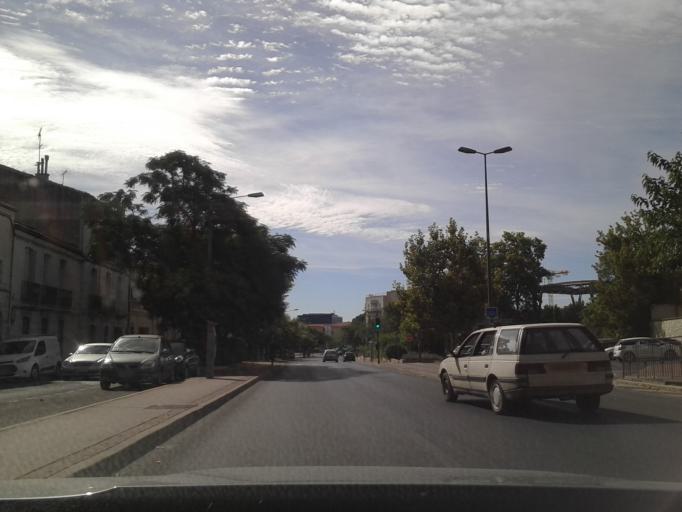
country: FR
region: Languedoc-Roussillon
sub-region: Departement de l'Herault
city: Montpellier
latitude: 43.6053
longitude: 3.8884
